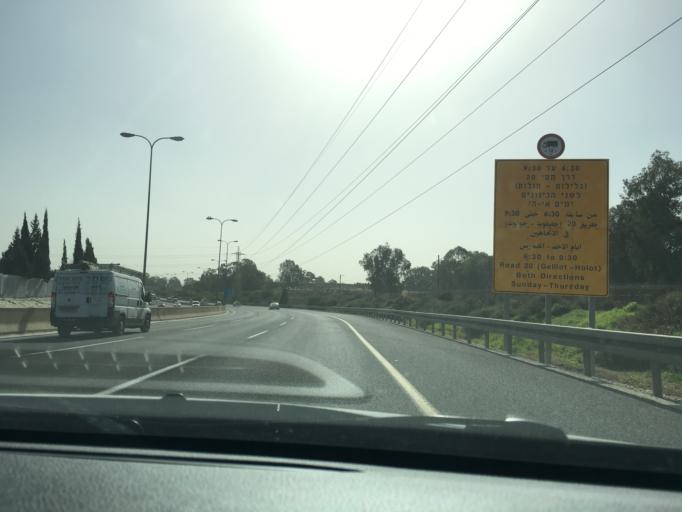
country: IL
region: Central District
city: Hod HaSharon
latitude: 32.1366
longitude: 34.8712
